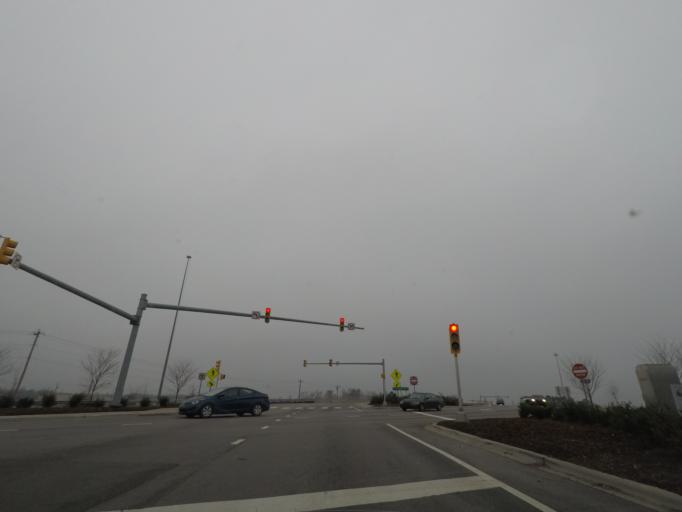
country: US
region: North Carolina
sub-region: Robeson County
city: Lumberton
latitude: 34.6693
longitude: -79.0051
